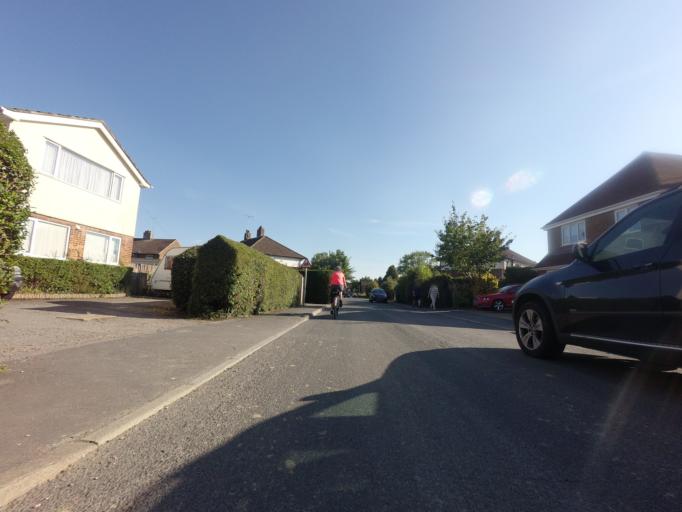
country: GB
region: England
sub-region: Kent
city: Tenterden
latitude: 51.0686
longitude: 0.7015
